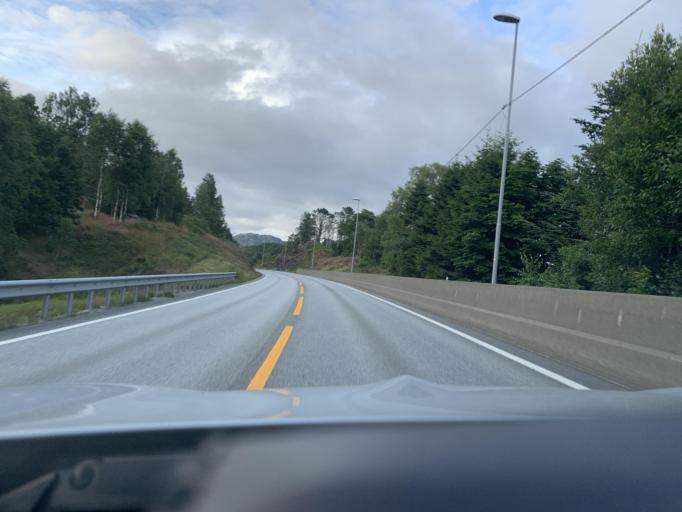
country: NO
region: Rogaland
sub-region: Bjerkreim
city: Vikesa
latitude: 58.5864
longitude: 6.0751
